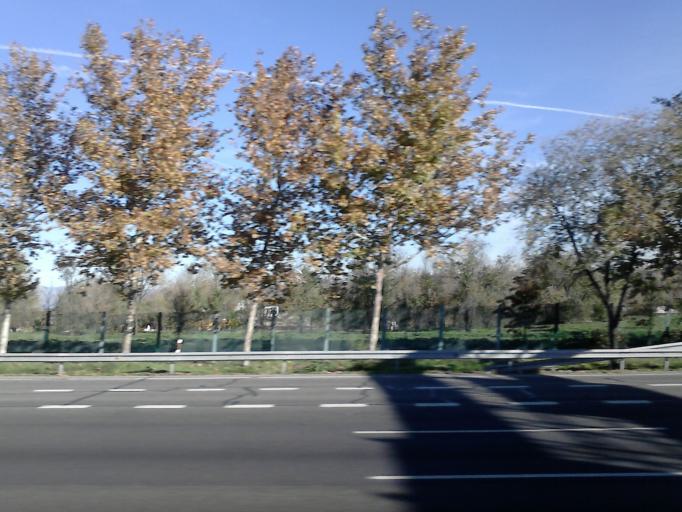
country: ES
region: Madrid
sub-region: Provincia de Madrid
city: Moncloa-Aravaca
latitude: 40.4603
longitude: -3.7546
